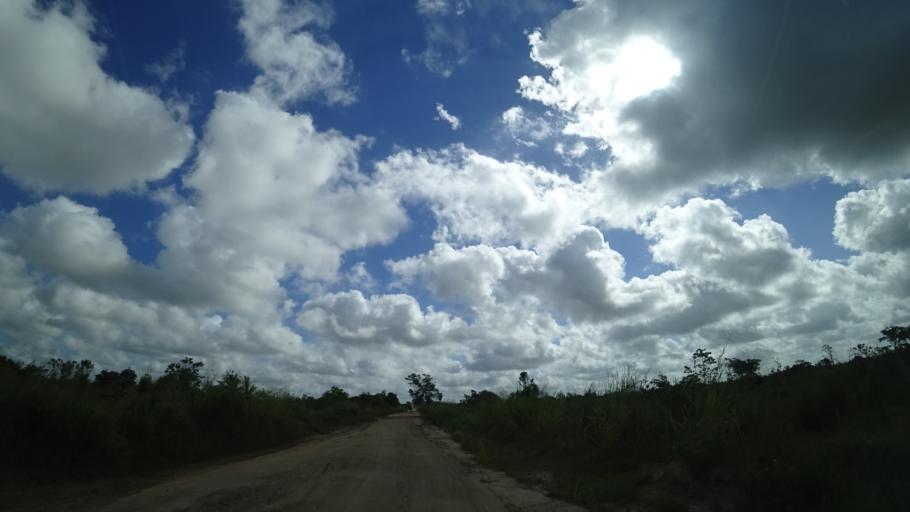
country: MZ
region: Sofala
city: Dondo
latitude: -19.4080
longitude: 34.7096
